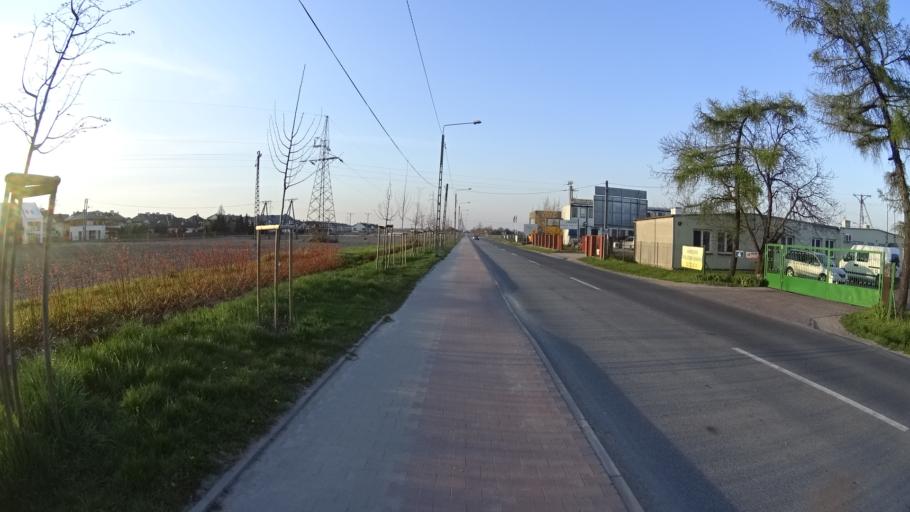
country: PL
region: Masovian Voivodeship
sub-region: Powiat warszawski zachodni
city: Ozarow Mazowiecki
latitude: 52.2113
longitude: 20.8107
